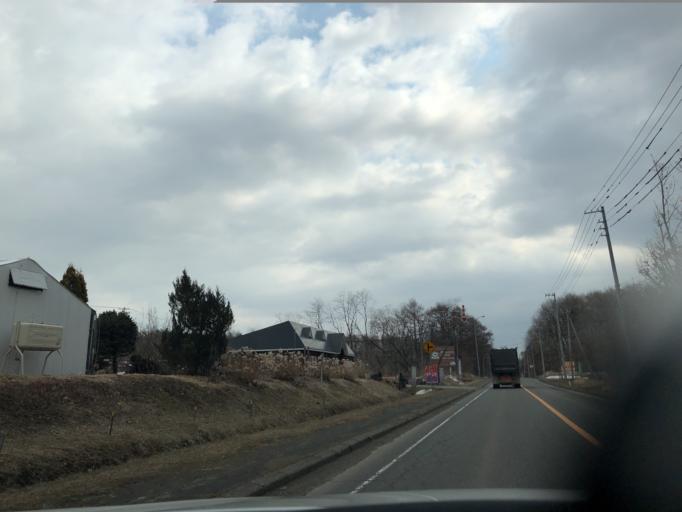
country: JP
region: Hokkaido
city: Chitose
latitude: 42.7601
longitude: 141.7838
